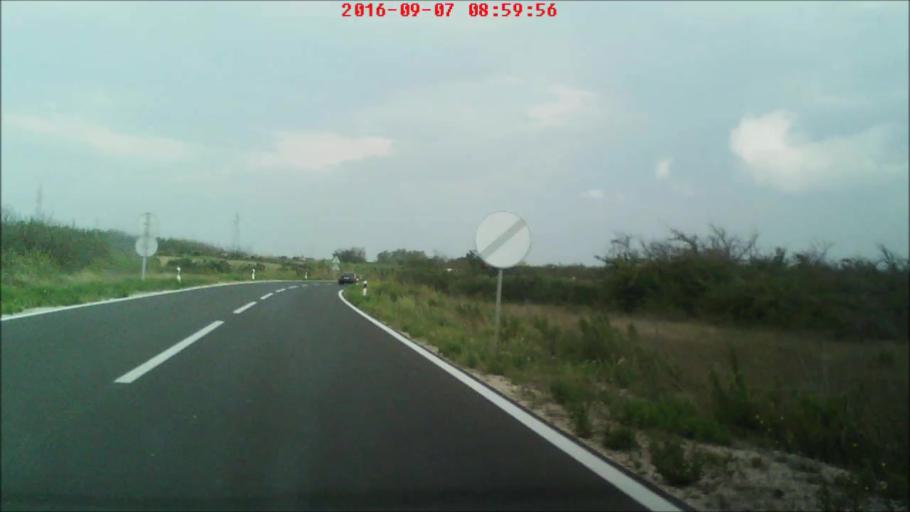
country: HR
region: Zadarska
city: Nin
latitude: 44.2463
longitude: 15.1670
